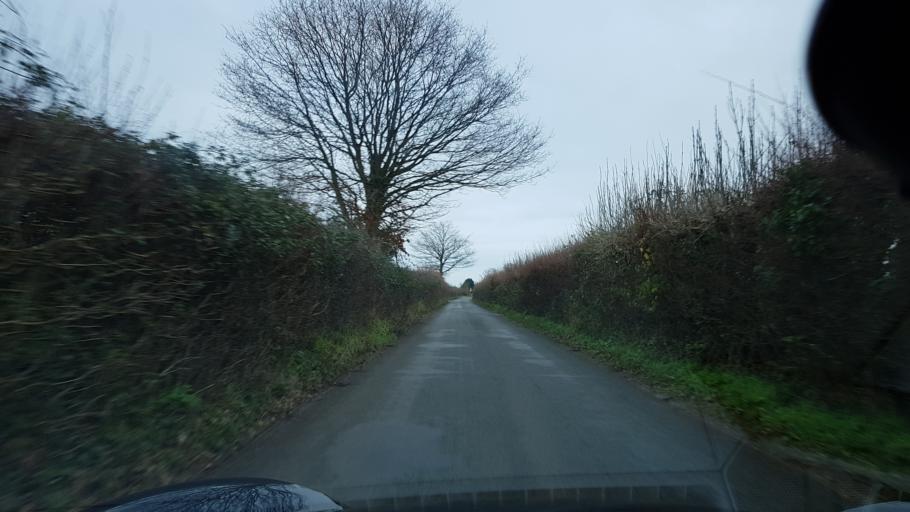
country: GB
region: England
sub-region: Somerset
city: Ilminster
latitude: 50.9392
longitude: -2.9551
